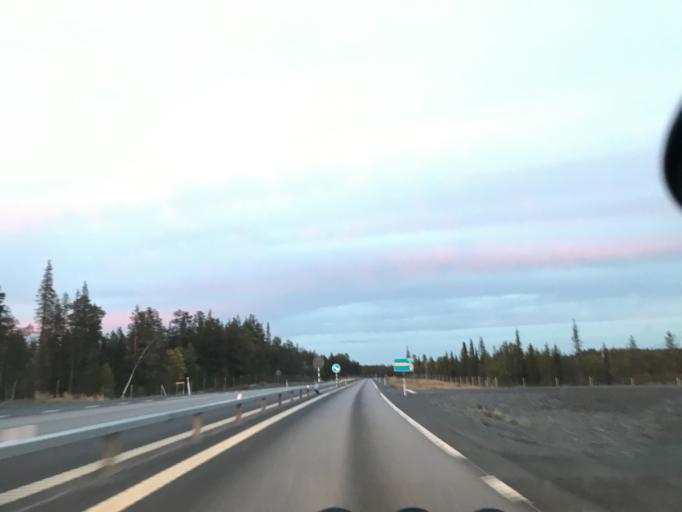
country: SE
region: Norrbotten
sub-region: Gallivare Kommun
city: Malmberget
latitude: 67.6718
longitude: 20.9318
